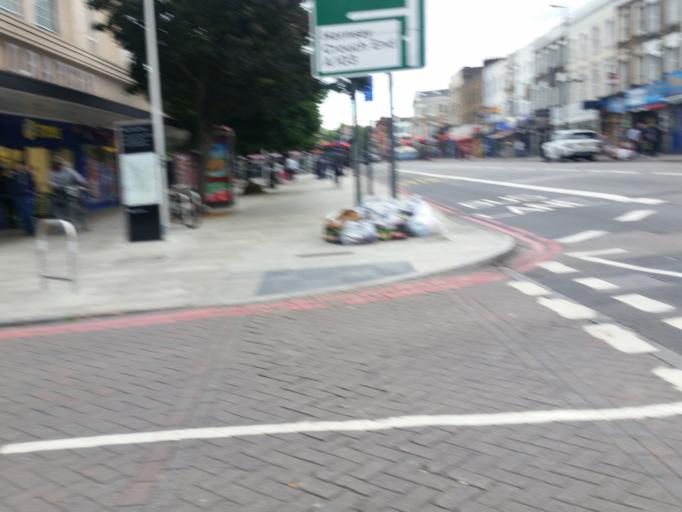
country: GB
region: England
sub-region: Greater London
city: Holloway
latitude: 51.5595
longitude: -0.1166
